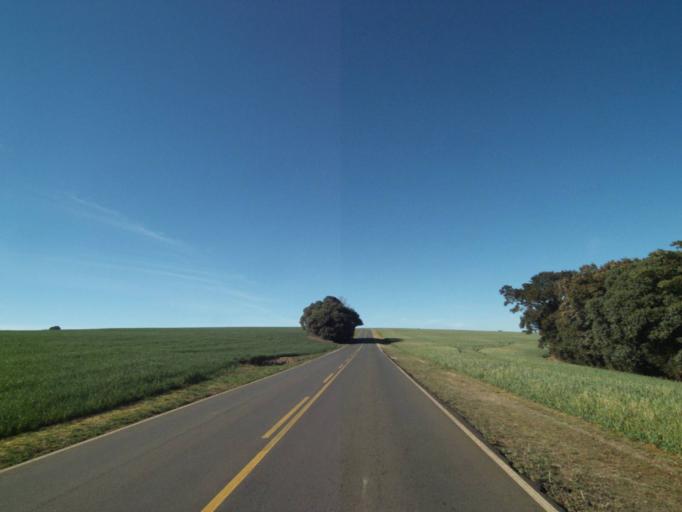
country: BR
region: Parana
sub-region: Tibagi
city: Tibagi
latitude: -24.5343
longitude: -50.3155
